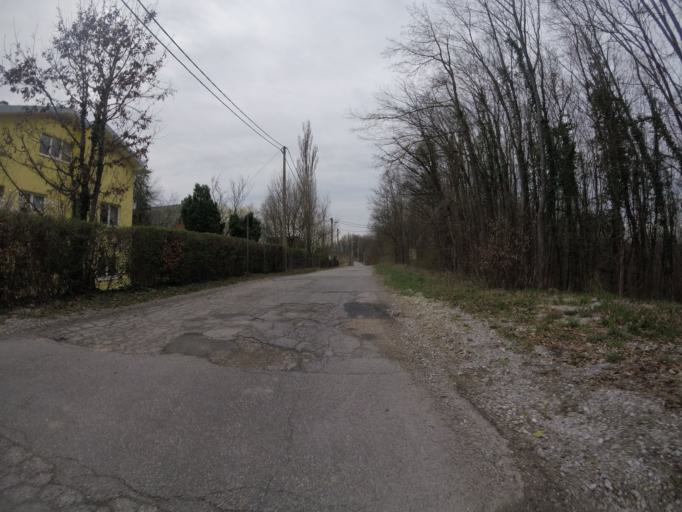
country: HR
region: Grad Zagreb
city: Strmec
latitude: 45.6320
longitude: 15.9361
